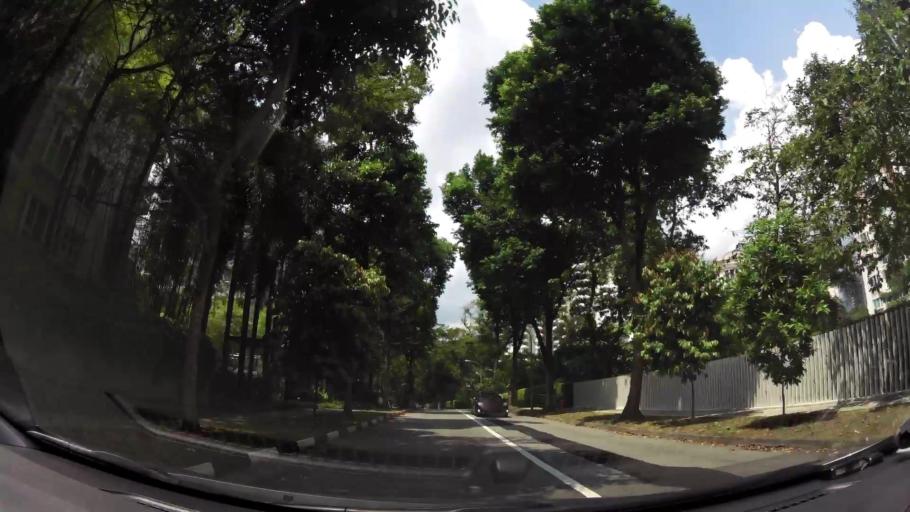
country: SG
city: Singapore
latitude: 1.2953
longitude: 103.8267
